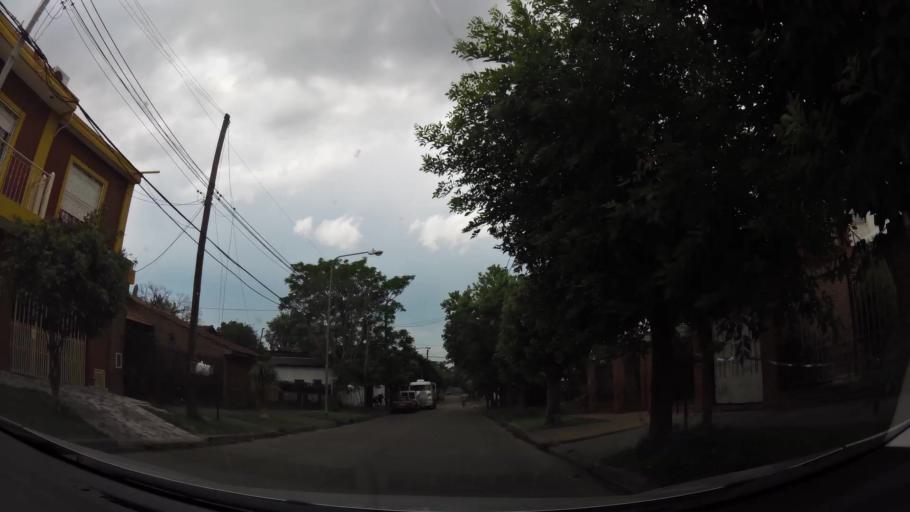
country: AR
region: Buenos Aires
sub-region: Partido de Tigre
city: Tigre
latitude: -34.4650
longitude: -58.6486
